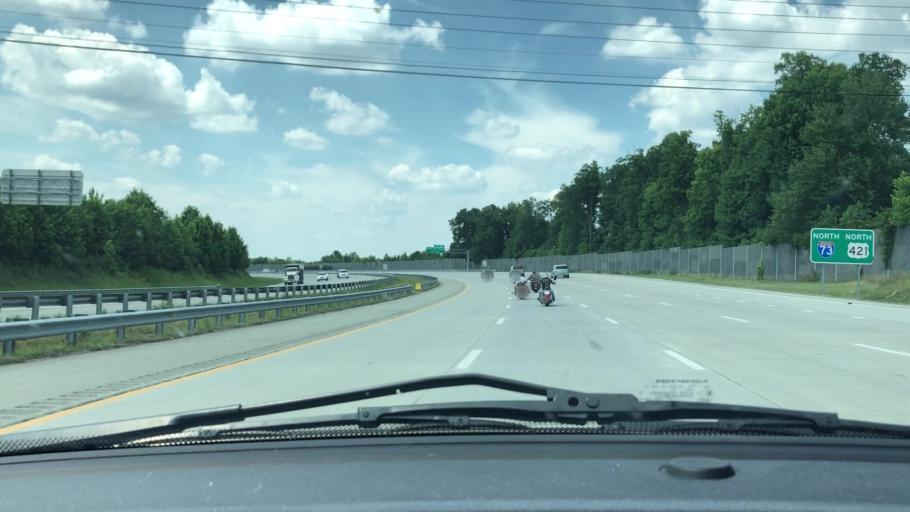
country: US
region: North Carolina
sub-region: Guilford County
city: Greensboro
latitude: 36.0161
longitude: -79.8530
